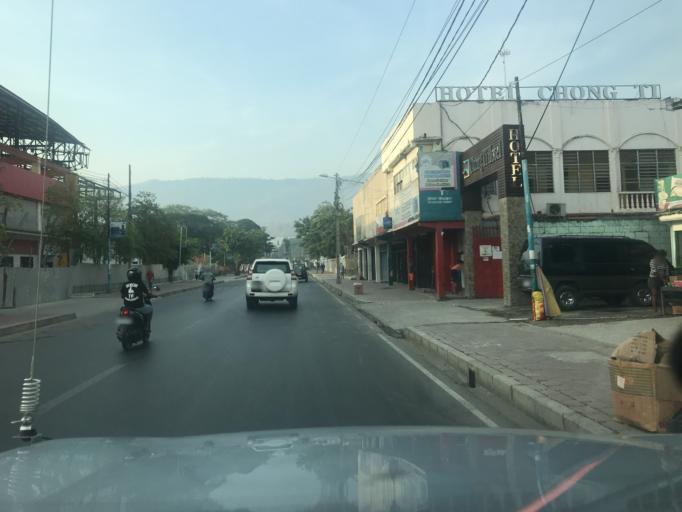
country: TL
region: Dili
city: Dili
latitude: -8.5573
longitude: 125.5798
